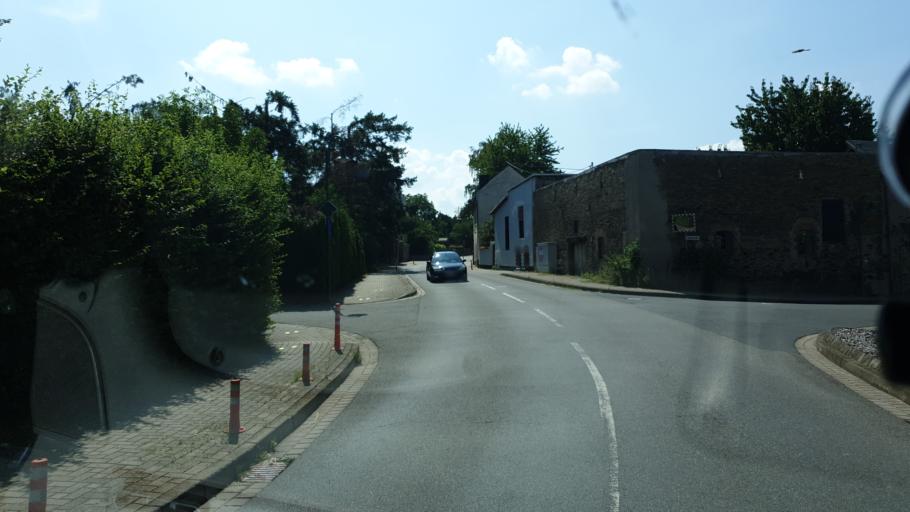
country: DE
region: Rheinland-Pfalz
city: Gierschnach
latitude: 50.2632
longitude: 7.3483
